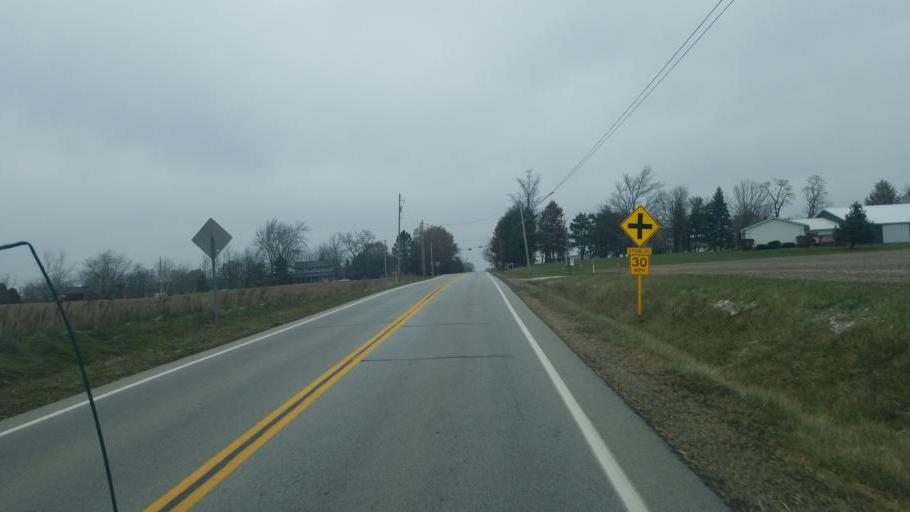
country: US
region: Ohio
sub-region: Medina County
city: Medina
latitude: 41.1533
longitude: -81.9252
